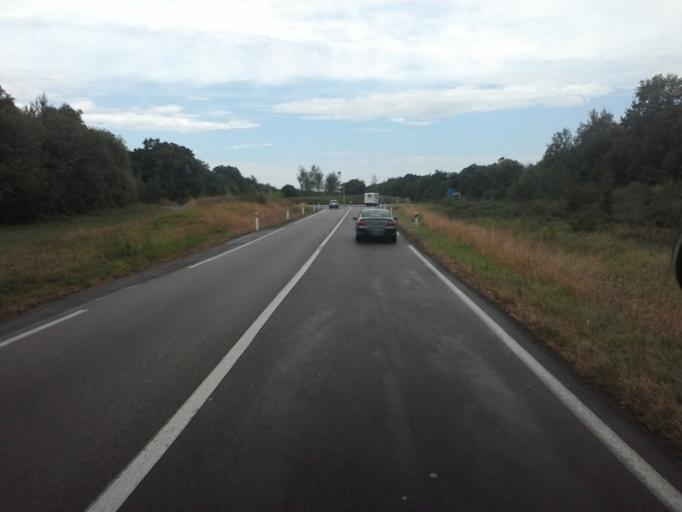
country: FR
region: Franche-Comte
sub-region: Departement du Jura
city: Poligny
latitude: 46.8425
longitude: 5.6225
